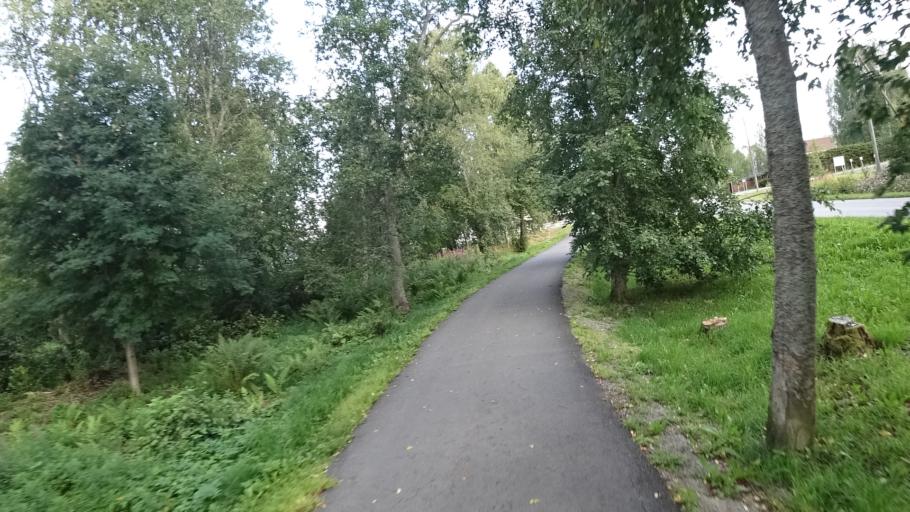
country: FI
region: North Karelia
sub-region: Joensuu
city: Ilomantsi
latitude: 62.6735
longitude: 30.9248
